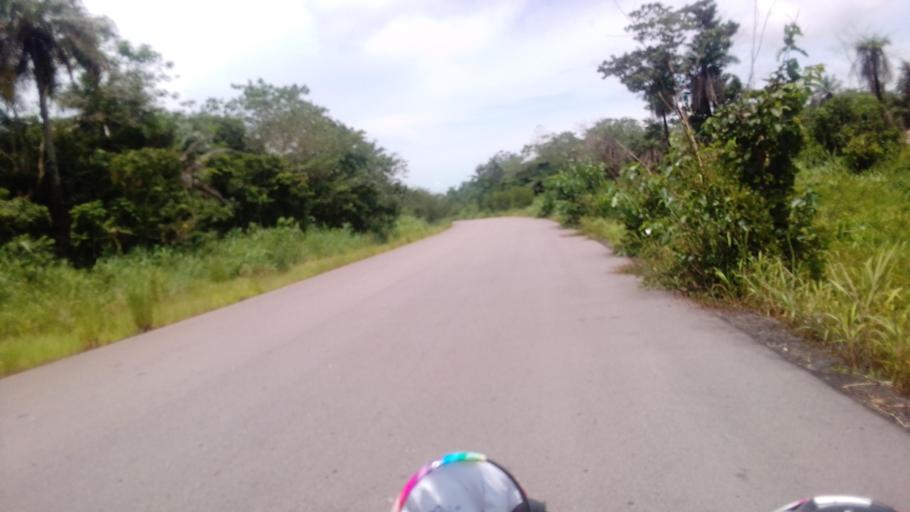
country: SL
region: Northern Province
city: Makeni
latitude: 9.0513
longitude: -12.1733
